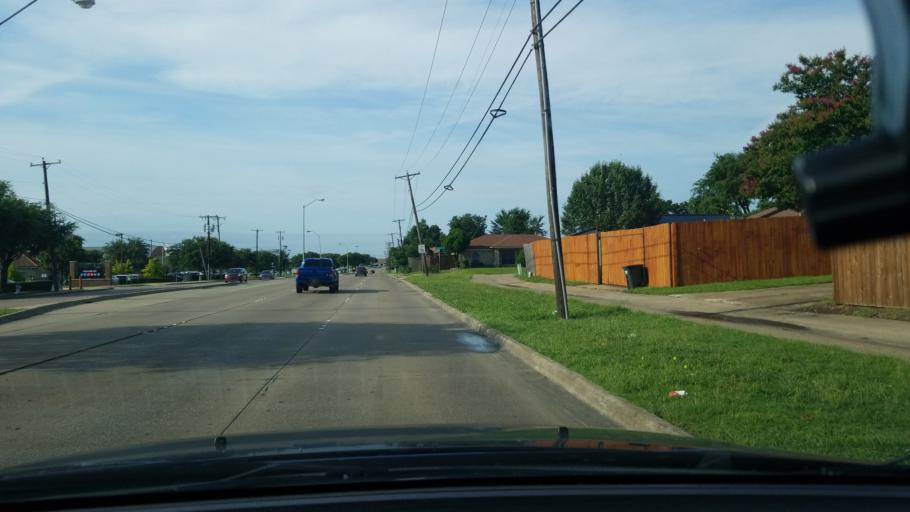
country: US
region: Texas
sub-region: Dallas County
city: Mesquite
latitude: 32.8042
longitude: -96.6113
